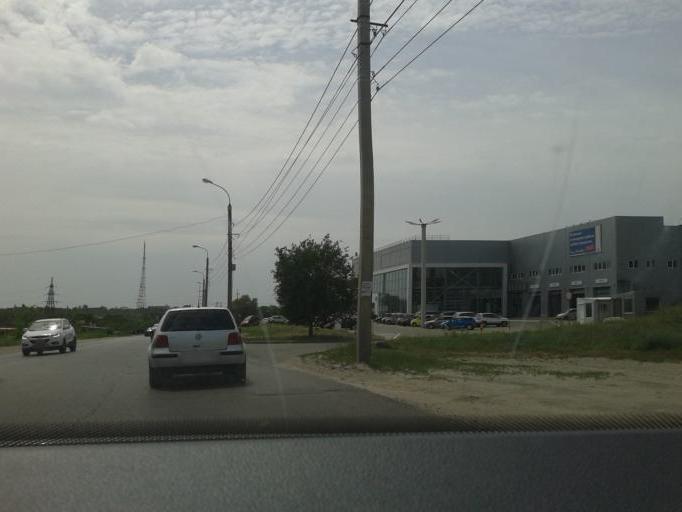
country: RU
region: Volgograd
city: Volgograd
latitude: 48.7576
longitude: 44.5230
